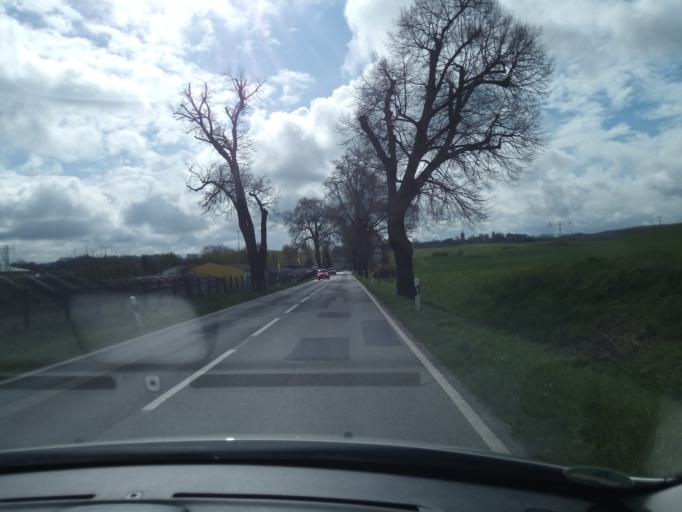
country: DE
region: Mecklenburg-Vorpommern
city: Burg Stargard
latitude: 53.5048
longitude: 13.2946
